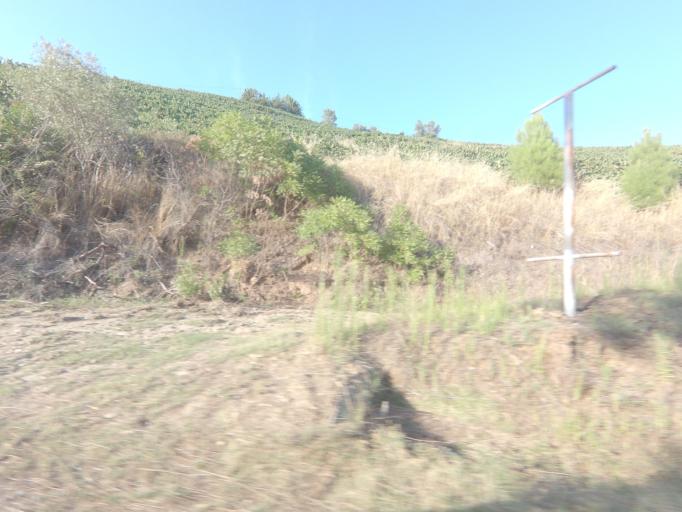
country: PT
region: Vila Real
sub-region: Sabrosa
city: Sabrosa
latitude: 41.2673
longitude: -7.5469
